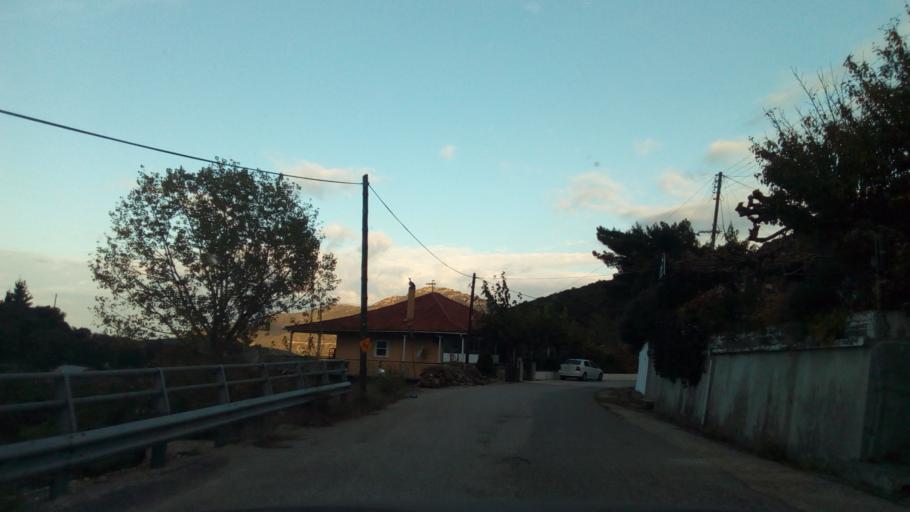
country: GR
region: West Greece
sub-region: Nomos Aitolias kai Akarnanias
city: Nafpaktos
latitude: 38.5194
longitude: 21.8437
